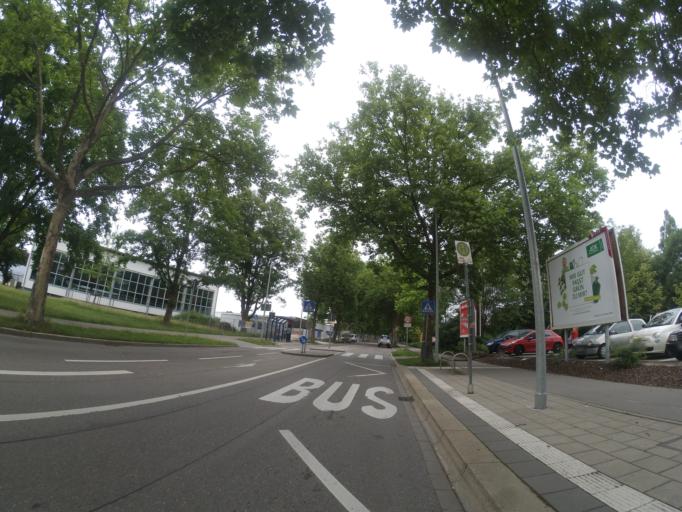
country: DE
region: Bavaria
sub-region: Swabia
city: Neu-Ulm
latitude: 48.3980
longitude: 10.0118
